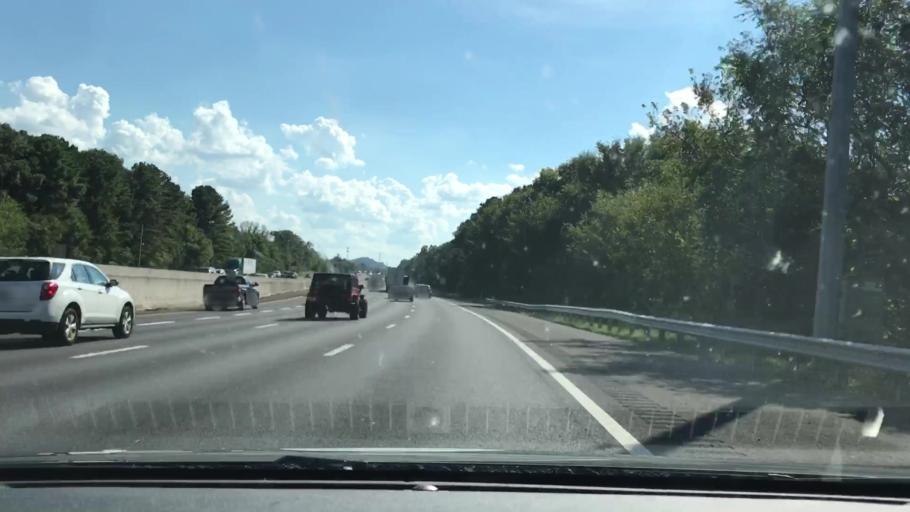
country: US
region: Tennessee
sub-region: Davidson County
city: Oak Hill
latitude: 36.0738
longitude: -86.7697
